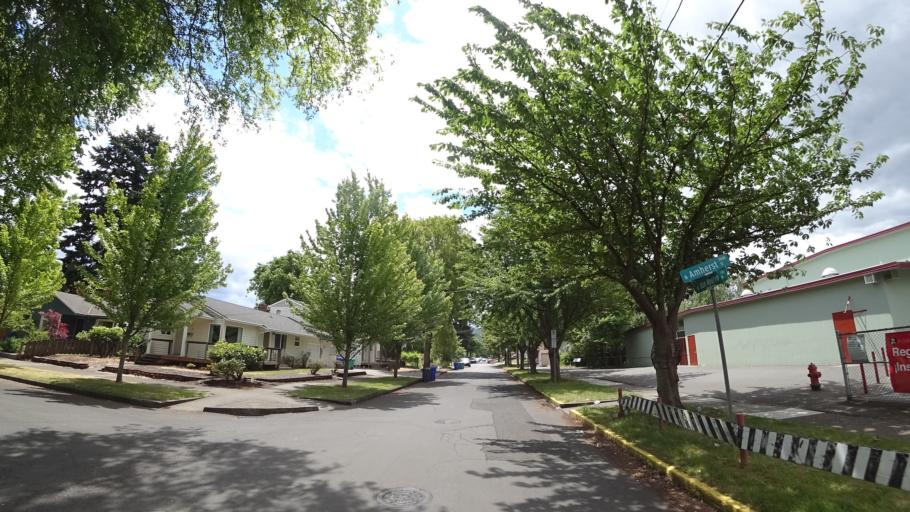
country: US
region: Oregon
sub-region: Washington County
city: West Haven
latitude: 45.5788
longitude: -122.7287
